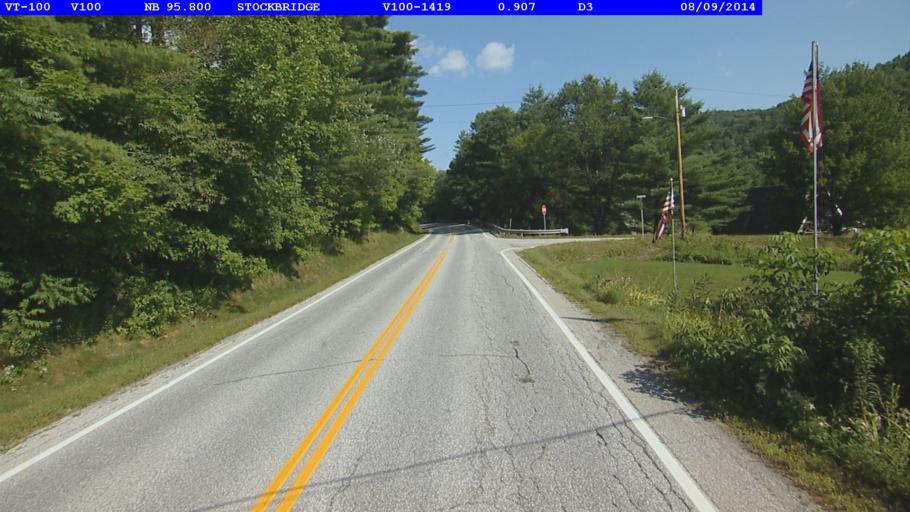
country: US
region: Vermont
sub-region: Orange County
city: Randolph
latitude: 43.7778
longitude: -72.7813
